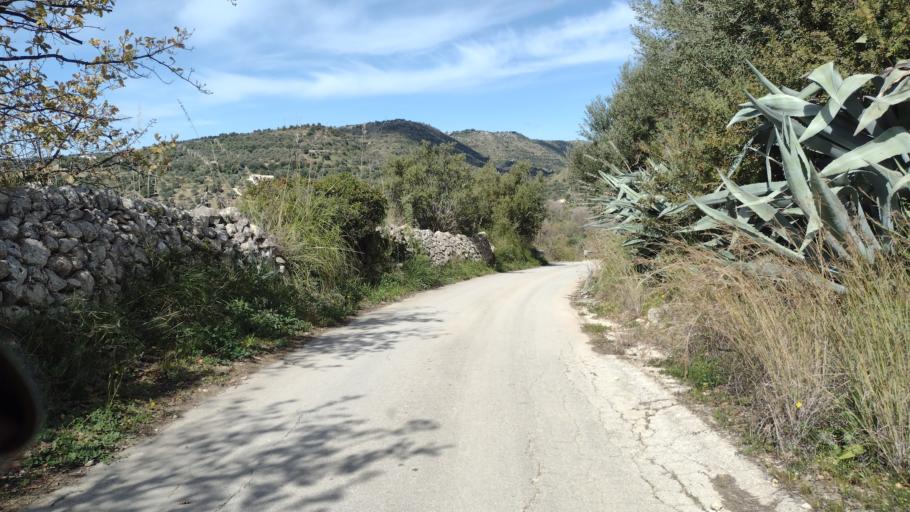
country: IT
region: Sicily
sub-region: Provincia di Siracusa
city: Noto
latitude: 36.9037
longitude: 15.0211
